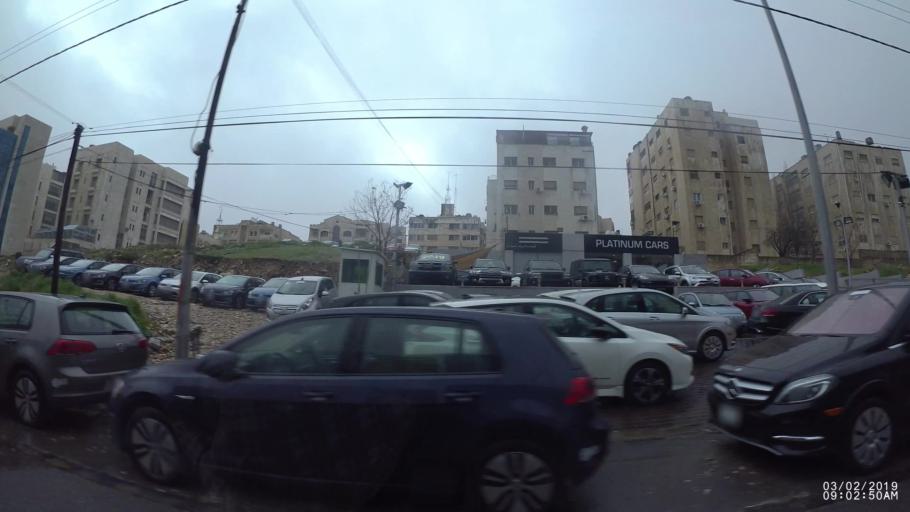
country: JO
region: Amman
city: Amman
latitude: 31.9616
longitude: 35.8908
